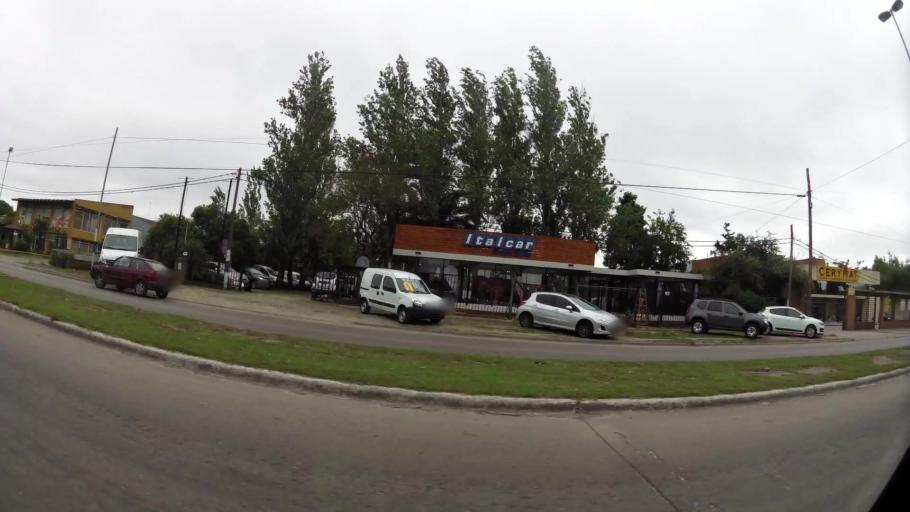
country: AR
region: Buenos Aires
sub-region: Partido de La Plata
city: La Plata
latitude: -34.9625
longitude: -58.0119
